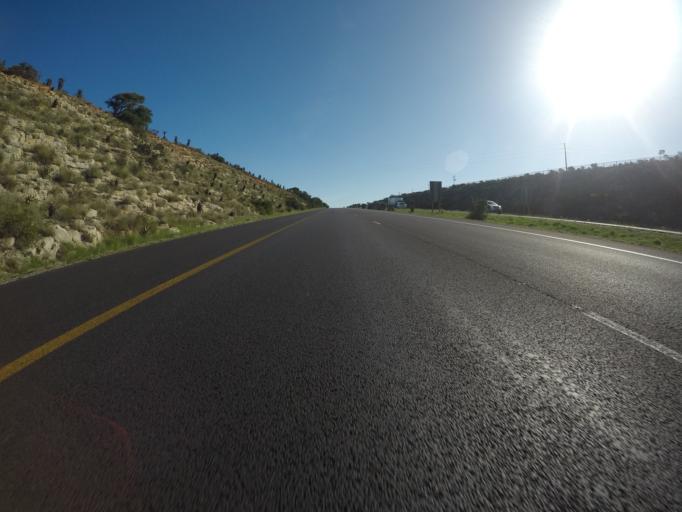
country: ZA
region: Western Cape
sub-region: Eden District Municipality
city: Mossel Bay
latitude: -34.1621
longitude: 22.0940
